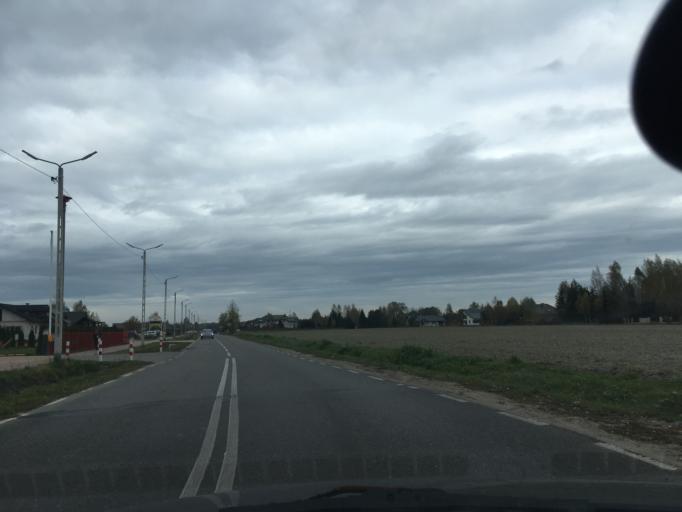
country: PL
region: Lodz Voivodeship
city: Zabia Wola
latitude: 52.0177
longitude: 20.7311
